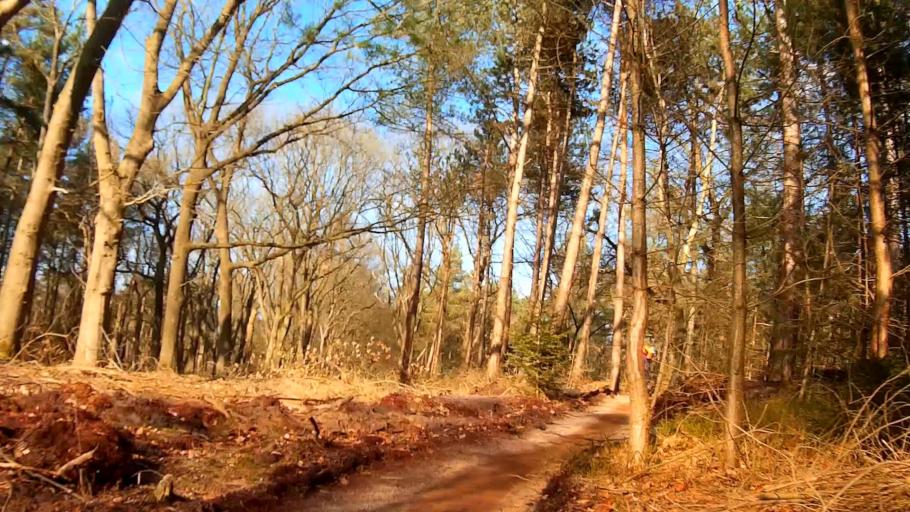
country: NL
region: Utrecht
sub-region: Gemeente Utrechtse Heuvelrug
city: Amerongen
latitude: 52.0249
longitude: 5.4609
